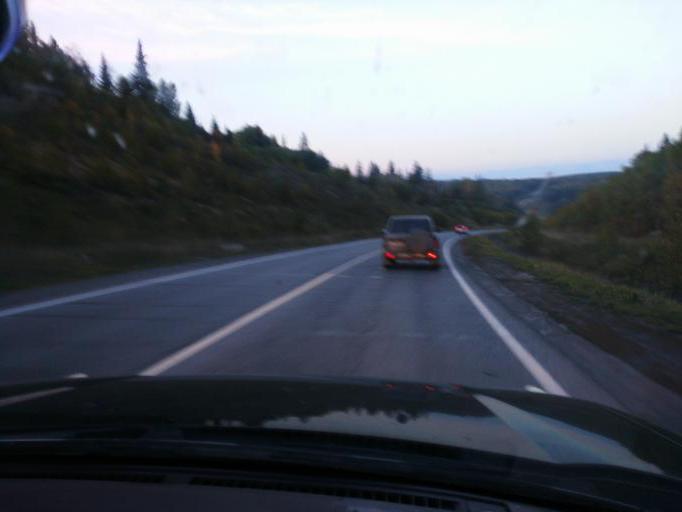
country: RU
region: Perm
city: Sylva
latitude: 58.2973
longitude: 56.7604
